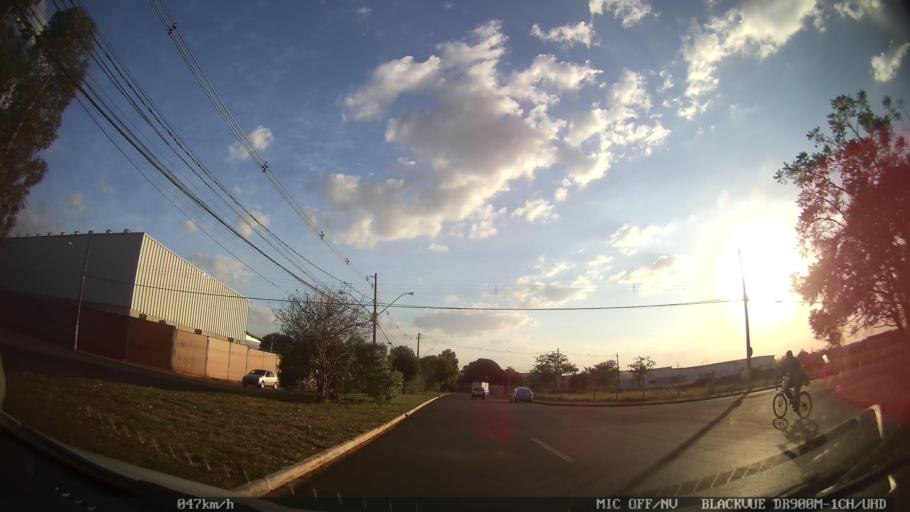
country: BR
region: Sao Paulo
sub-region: Ribeirao Preto
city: Ribeirao Preto
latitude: -21.1625
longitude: -47.7401
